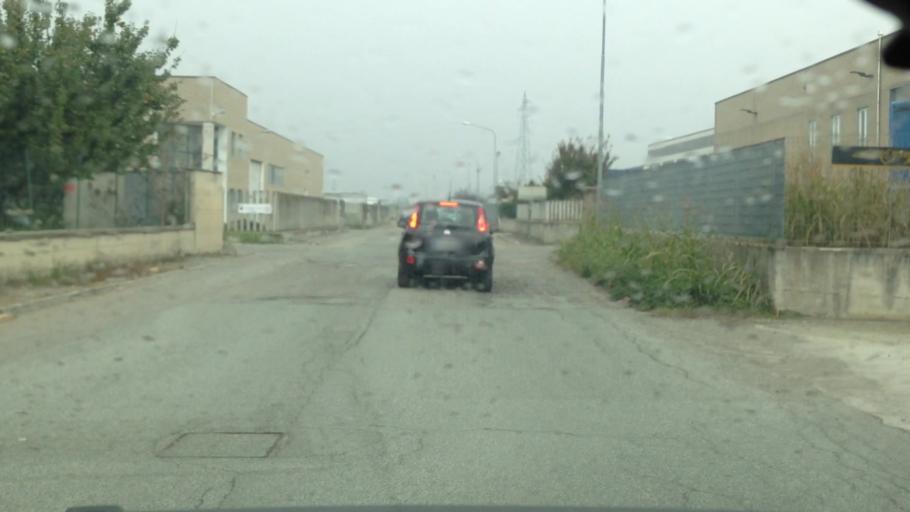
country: IT
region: Piedmont
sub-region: Provincia di Alessandria
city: Solero
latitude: 44.9156
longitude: 8.4828
